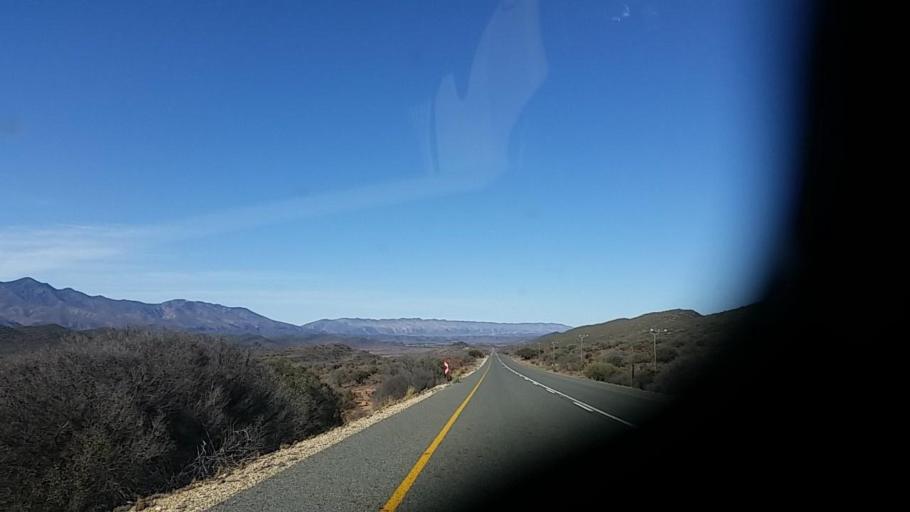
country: ZA
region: Western Cape
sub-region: Eden District Municipality
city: Knysna
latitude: -33.5224
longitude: 22.9456
